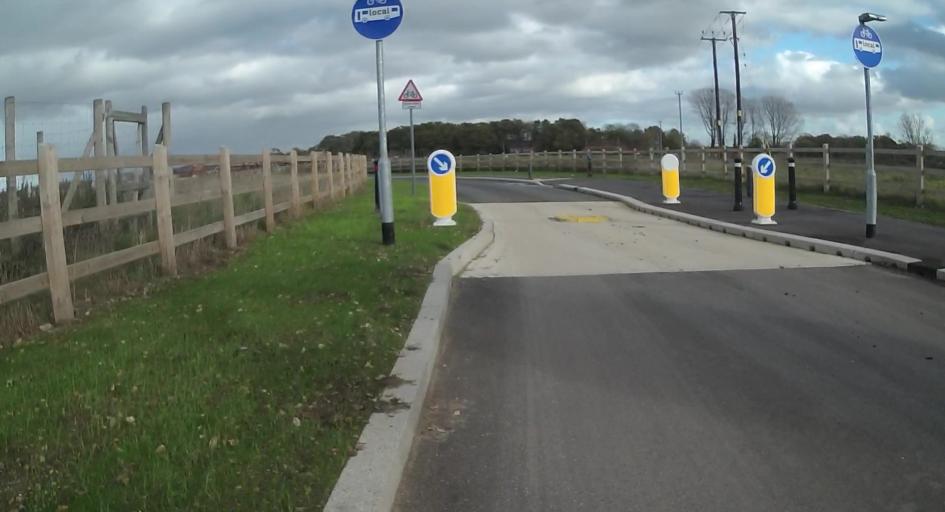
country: GB
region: England
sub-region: Wokingham
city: Shinfield
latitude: 51.3988
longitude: -0.9581
